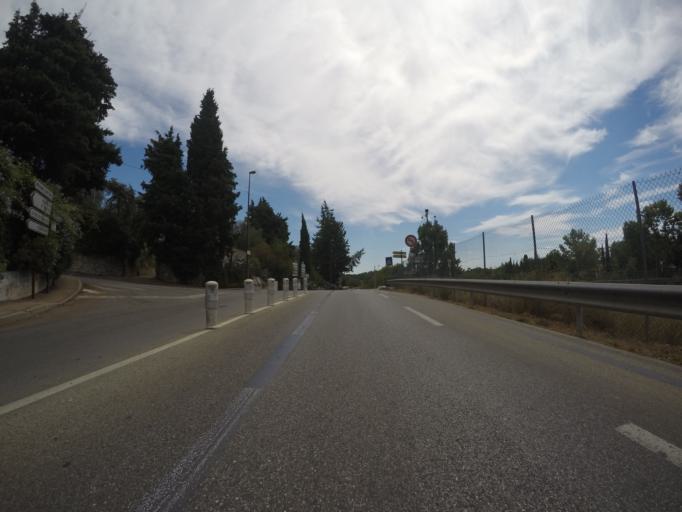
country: FR
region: Provence-Alpes-Cote d'Azur
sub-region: Departement des Alpes-Maritimes
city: Mougins
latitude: 43.6053
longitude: 6.9996
